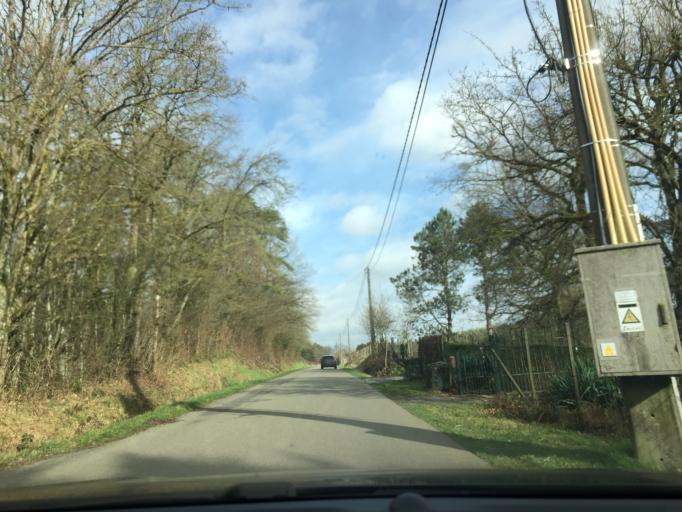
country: BE
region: Wallonia
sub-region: Province du Luxembourg
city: Hotton
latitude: 50.2943
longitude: 5.4888
